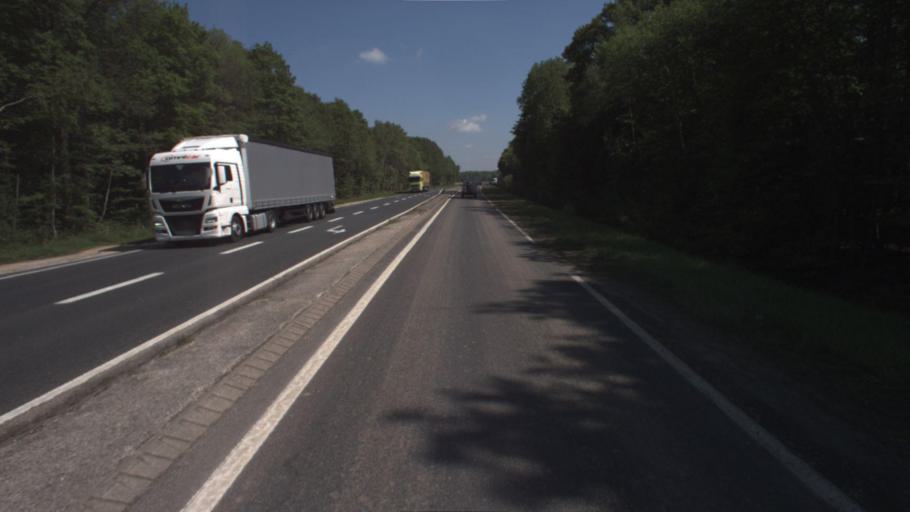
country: FR
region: Ile-de-France
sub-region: Departement de Seine-et-Marne
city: Chaumes-en-Brie
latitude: 48.6943
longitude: 2.8211
